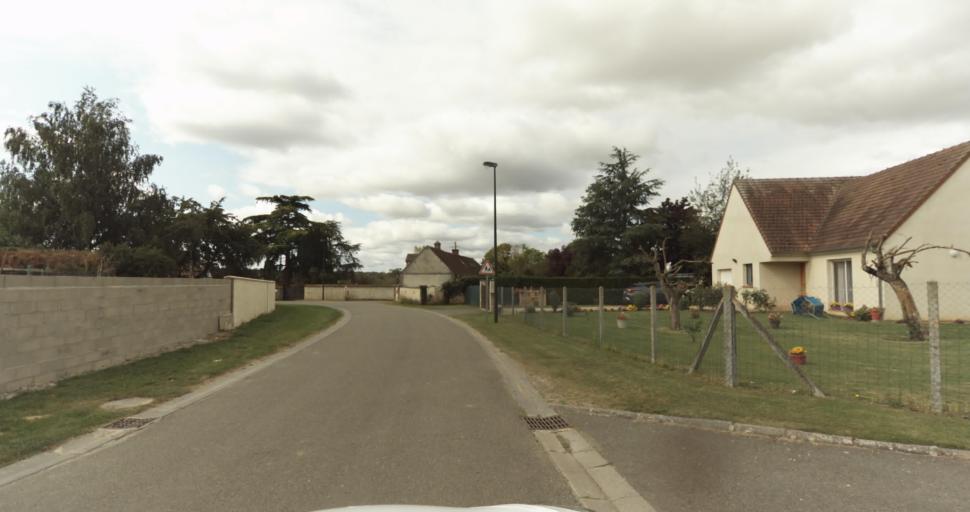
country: FR
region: Haute-Normandie
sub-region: Departement de l'Eure
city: Tillieres-sur-Avre
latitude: 48.7815
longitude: 1.1034
